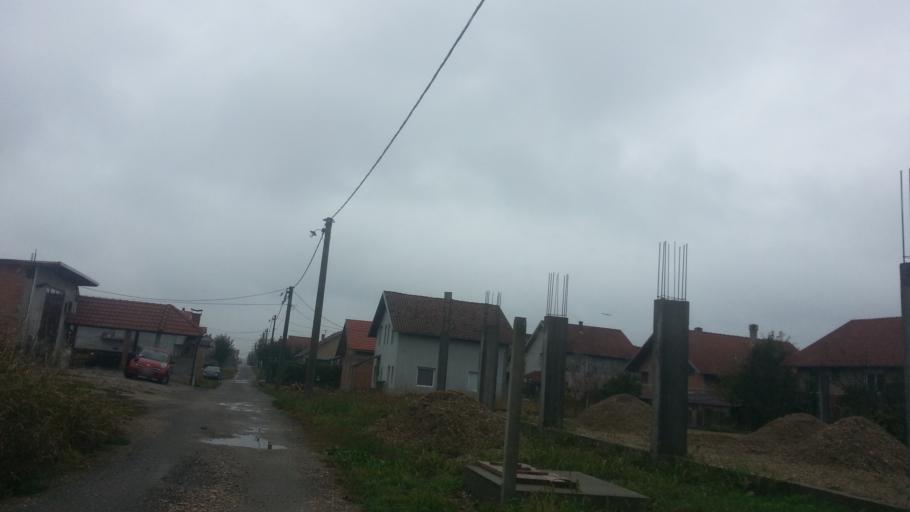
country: RS
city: Novi Banovci
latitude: 44.9101
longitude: 20.2927
